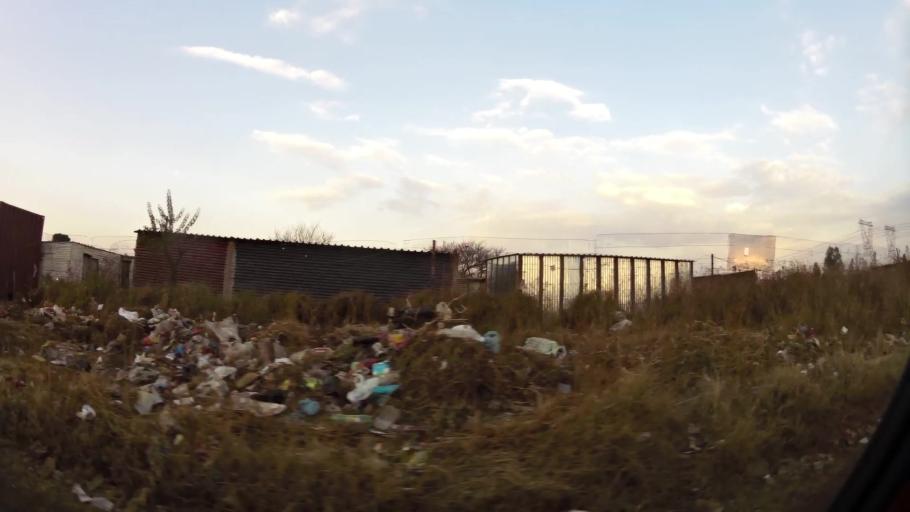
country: ZA
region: Gauteng
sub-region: City of Johannesburg Metropolitan Municipality
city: Orange Farm
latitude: -26.5546
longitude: 27.8397
